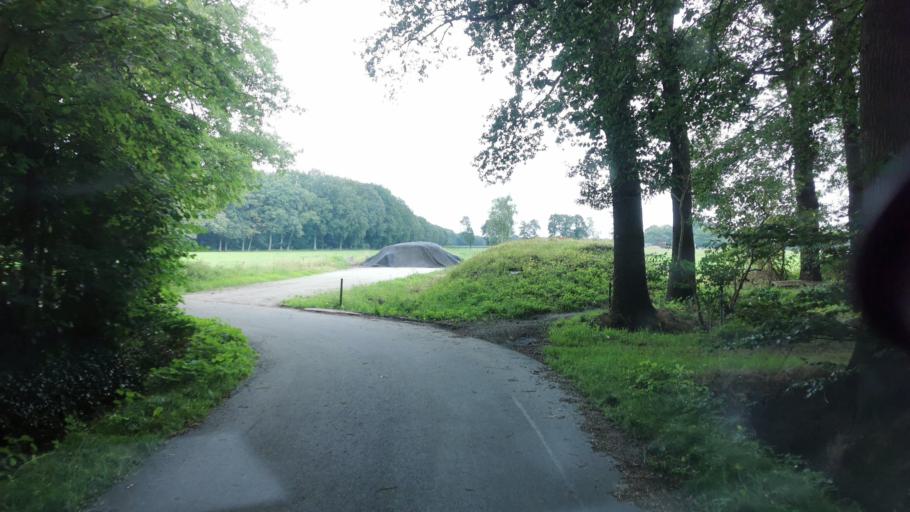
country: NL
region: Overijssel
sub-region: Gemeente Losser
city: Losser
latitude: 52.2482
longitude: 6.9737
